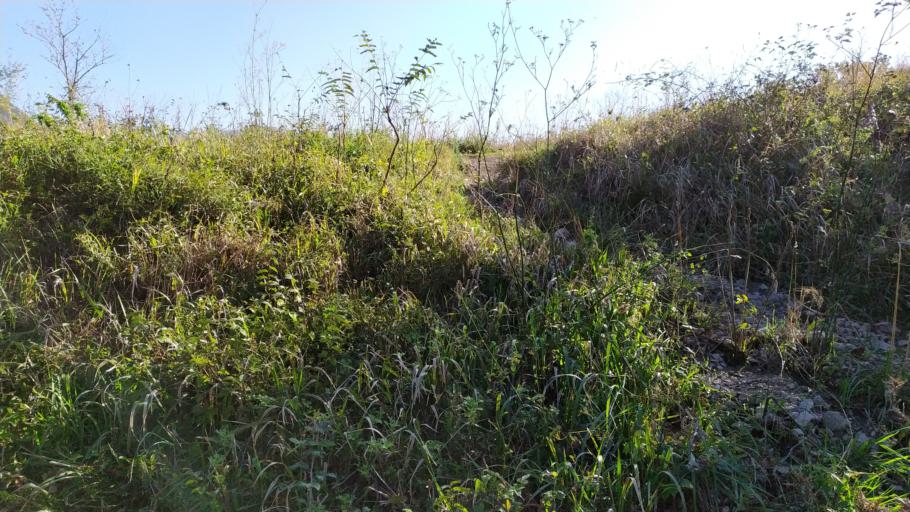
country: IT
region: Campania
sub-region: Provincia di Salerno
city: Siano
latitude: 40.8057
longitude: 14.6686
